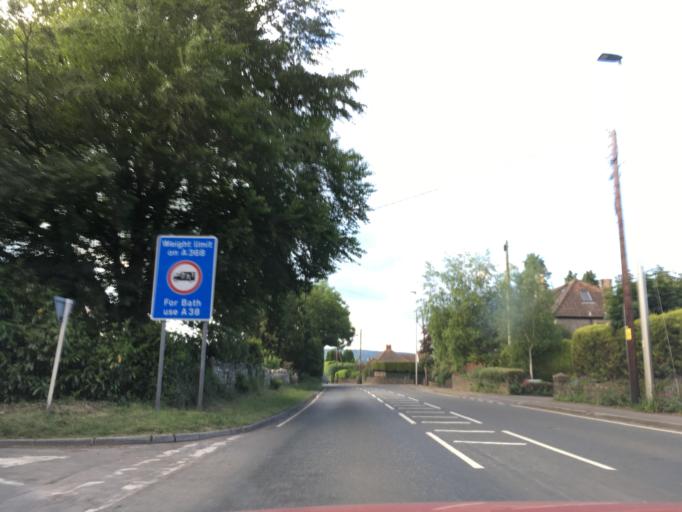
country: GB
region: England
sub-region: North Somerset
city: Churchill
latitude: 51.3317
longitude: -2.7948
